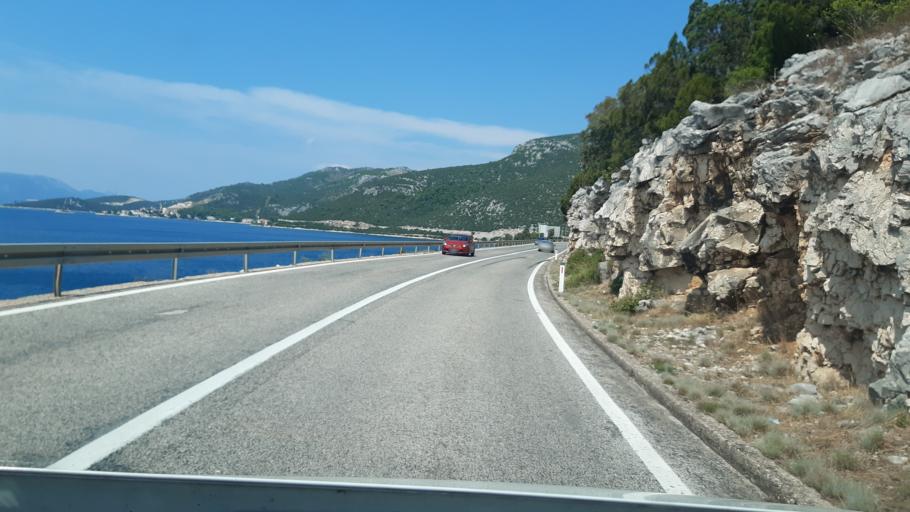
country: BA
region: Federation of Bosnia and Herzegovina
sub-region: Hercegovacko-Bosanski Kanton
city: Neum
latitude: 42.9355
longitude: 17.5840
